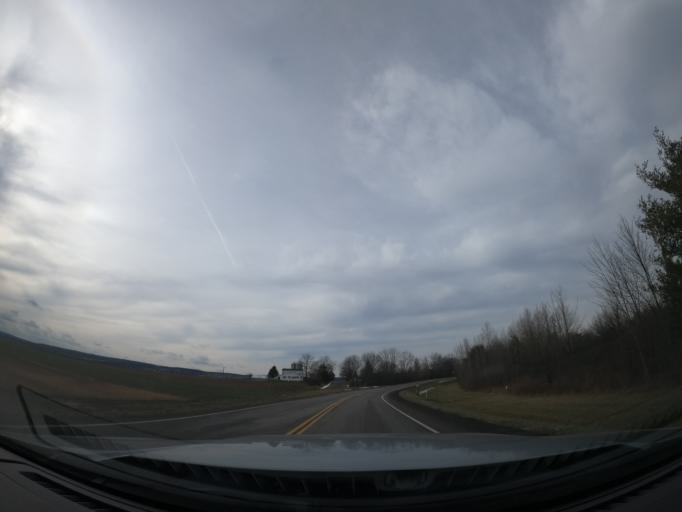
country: US
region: New York
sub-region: Yates County
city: Dundee
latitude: 42.4994
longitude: -76.9487
